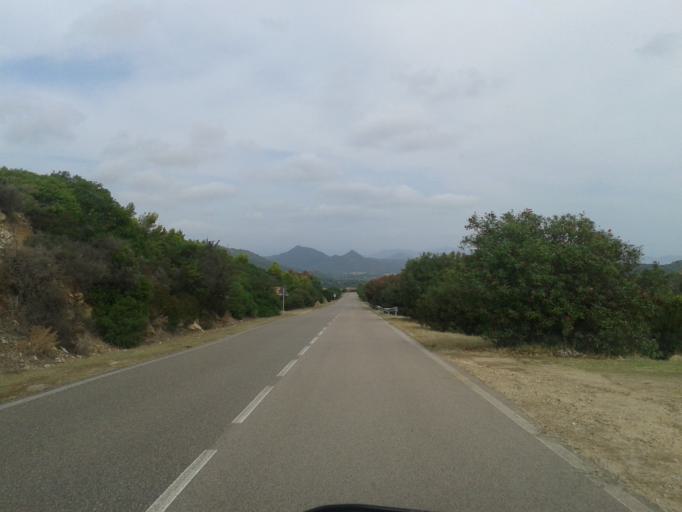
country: IT
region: Sardinia
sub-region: Provincia di Cagliari
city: Villasimius
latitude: 39.1622
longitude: 9.5630
